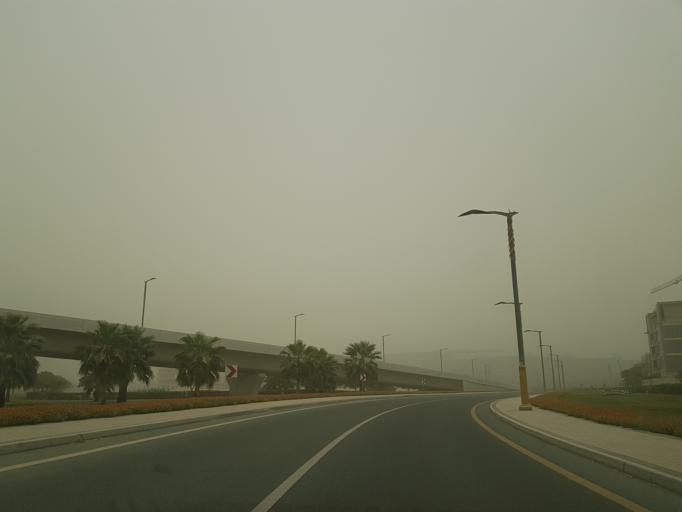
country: AE
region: Dubai
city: Dubai
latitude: 25.1560
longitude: 55.2912
